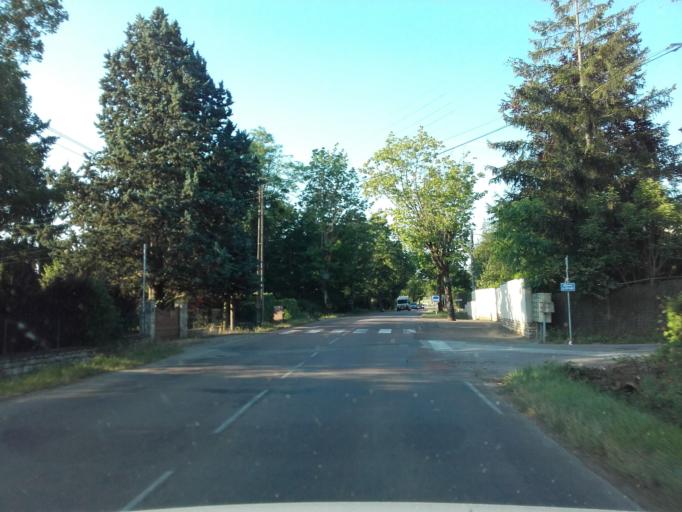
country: FR
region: Bourgogne
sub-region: Departement de Saone-et-Loire
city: Givry
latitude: 46.7701
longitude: 4.7383
